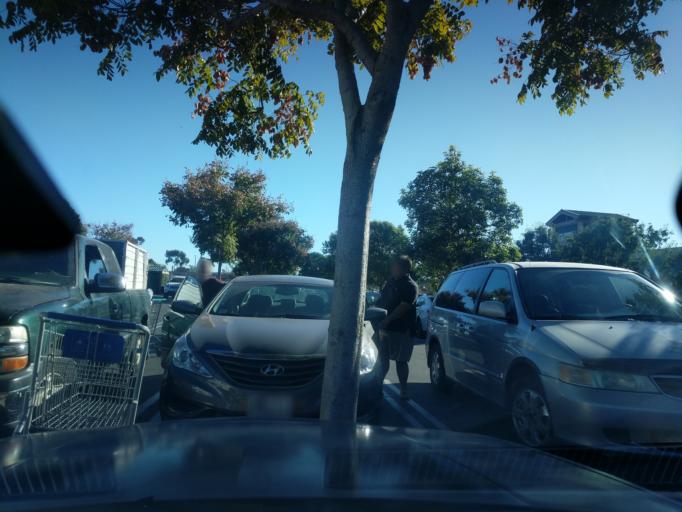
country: US
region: California
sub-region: Santa Barbara County
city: Goleta
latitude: 34.4421
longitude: -119.8319
